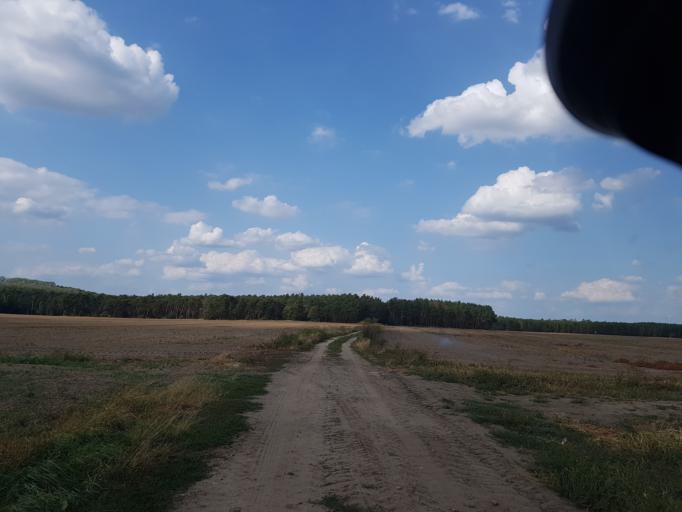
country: DE
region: Brandenburg
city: Calau
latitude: 51.7579
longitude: 13.9513
